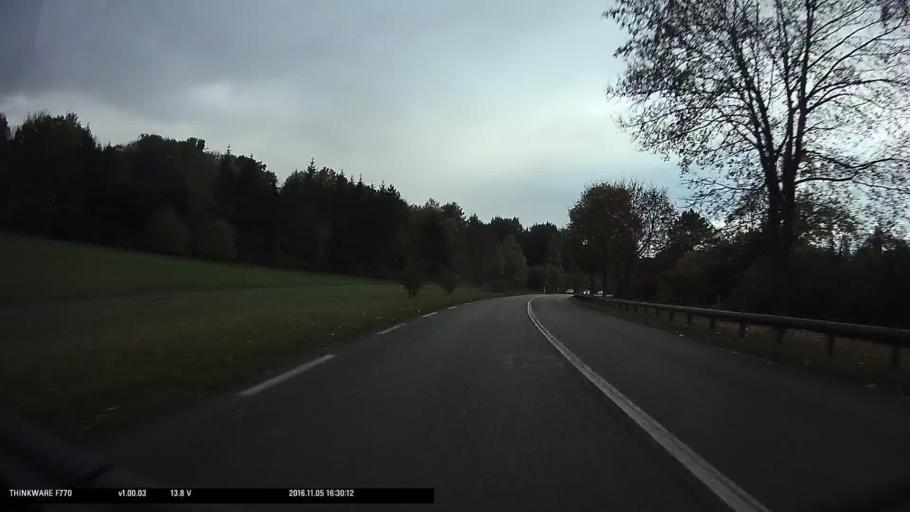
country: FR
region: Ile-de-France
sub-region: Departement du Val-d'Oise
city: Sagy
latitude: 49.0428
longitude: 1.9520
